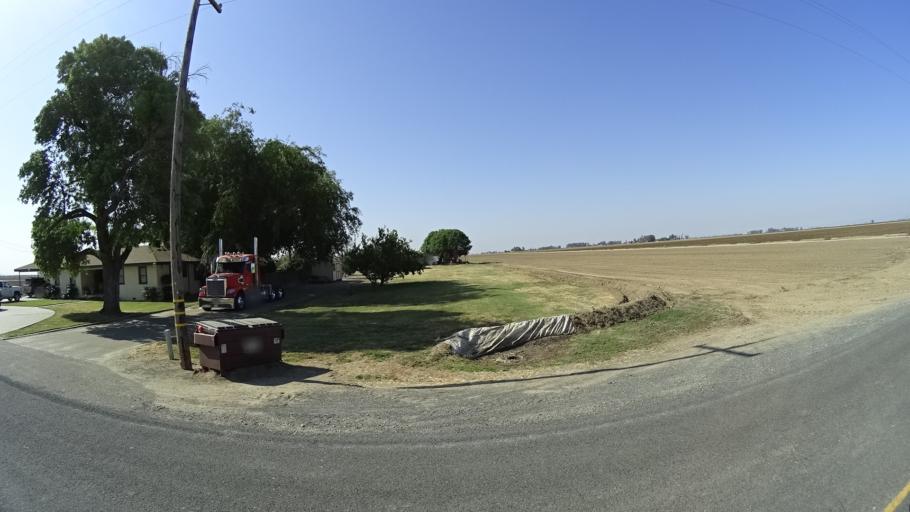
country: US
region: California
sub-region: Kings County
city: Home Garden
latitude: 36.2404
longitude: -119.6278
